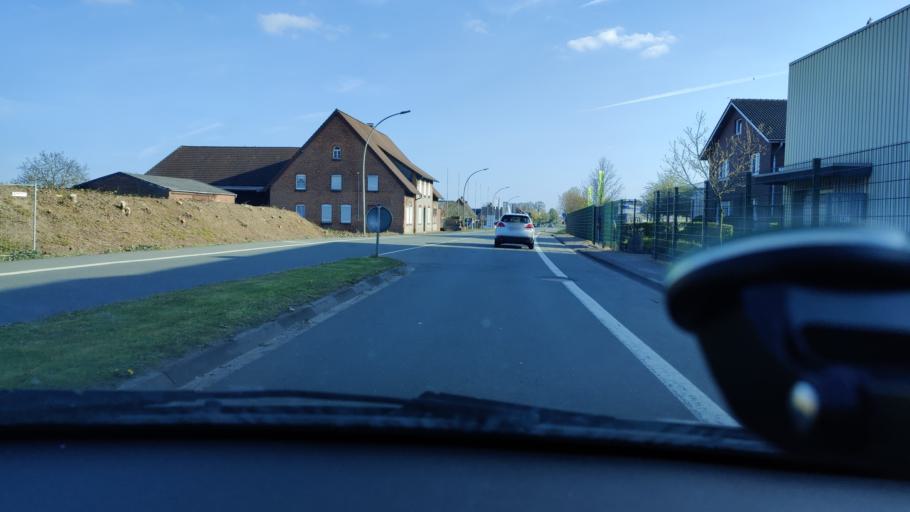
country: DE
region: North Rhine-Westphalia
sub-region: Regierungsbezirk Munster
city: Klein Reken
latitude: 51.8262
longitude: 7.0473
